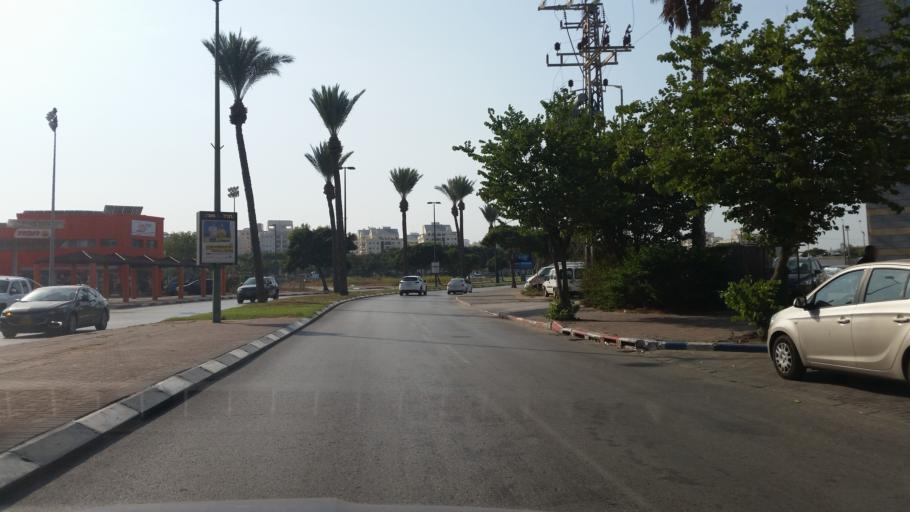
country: IL
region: Central District
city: Bet Yizhaq
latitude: 32.3141
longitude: 34.8735
